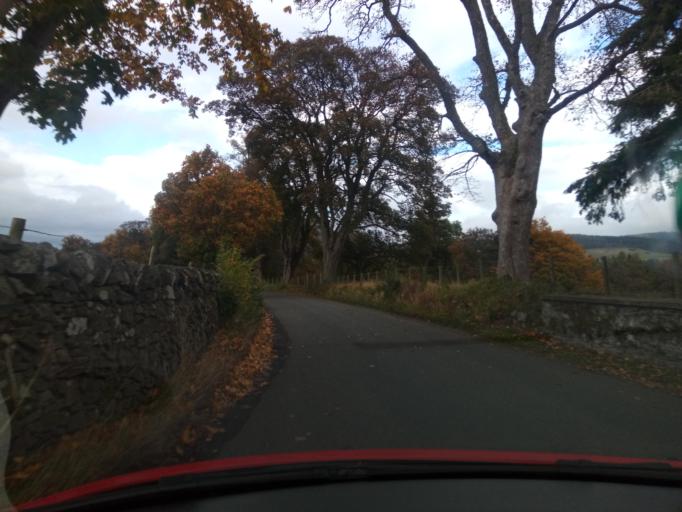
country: GB
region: Scotland
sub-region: The Scottish Borders
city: Peebles
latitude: 55.6383
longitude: -3.1475
